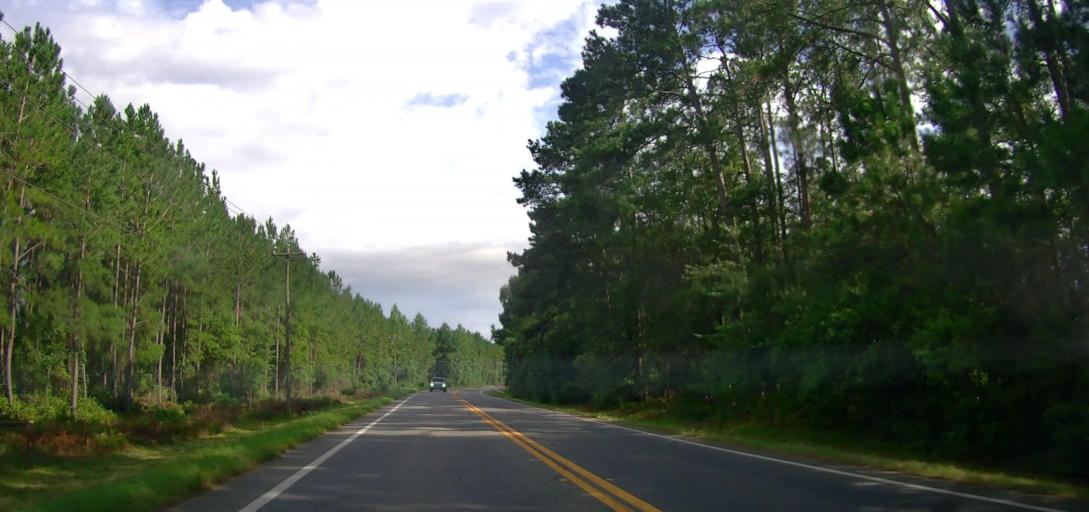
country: US
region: Georgia
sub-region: Coffee County
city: Douglas
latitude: 31.4551
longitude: -82.8882
